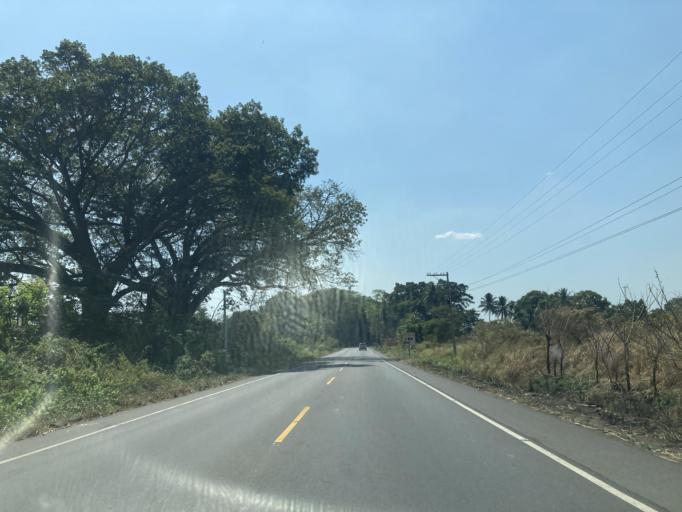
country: GT
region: Escuintla
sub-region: Municipio de Escuintla
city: Escuintla
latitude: 14.2472
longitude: -90.7411
